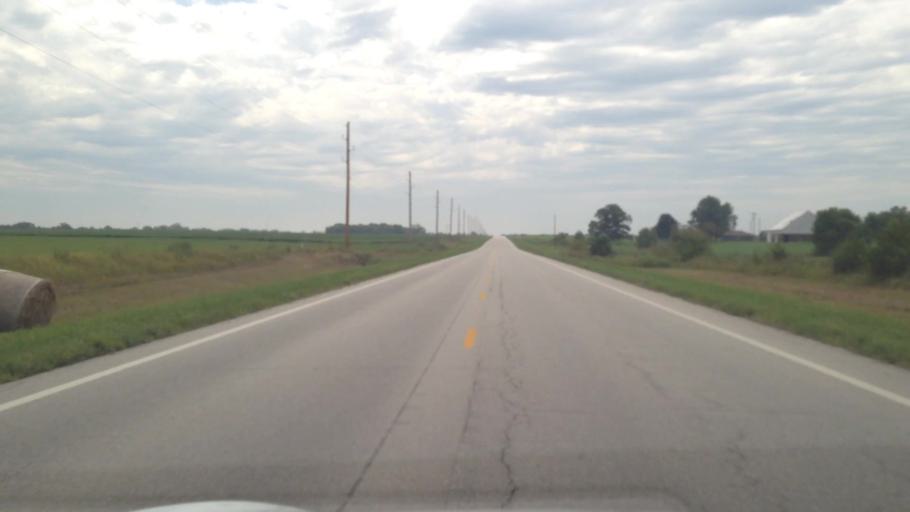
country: US
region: Kansas
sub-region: Allen County
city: Iola
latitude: 37.9431
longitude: -95.1700
